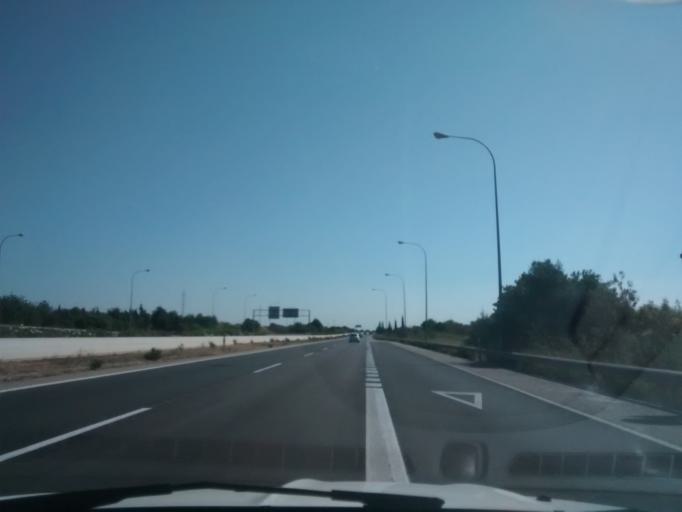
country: ES
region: Balearic Islands
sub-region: Illes Balears
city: Consell
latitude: 39.6700
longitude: 2.8262
